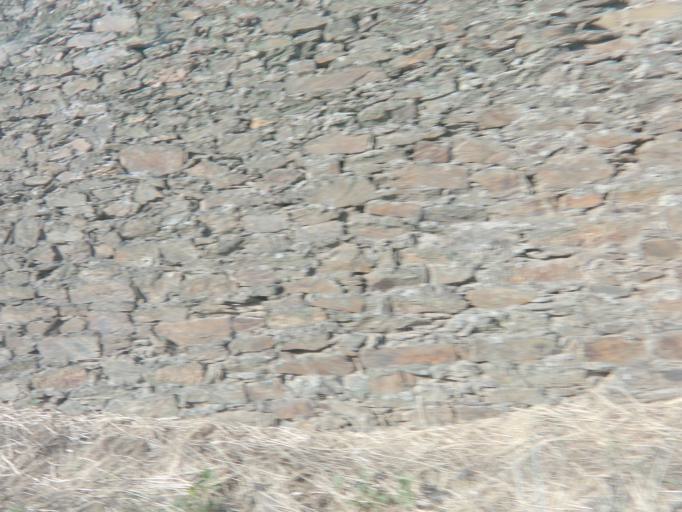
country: PT
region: Vila Real
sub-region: Sabrosa
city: Vilela
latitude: 41.1849
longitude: -7.5874
